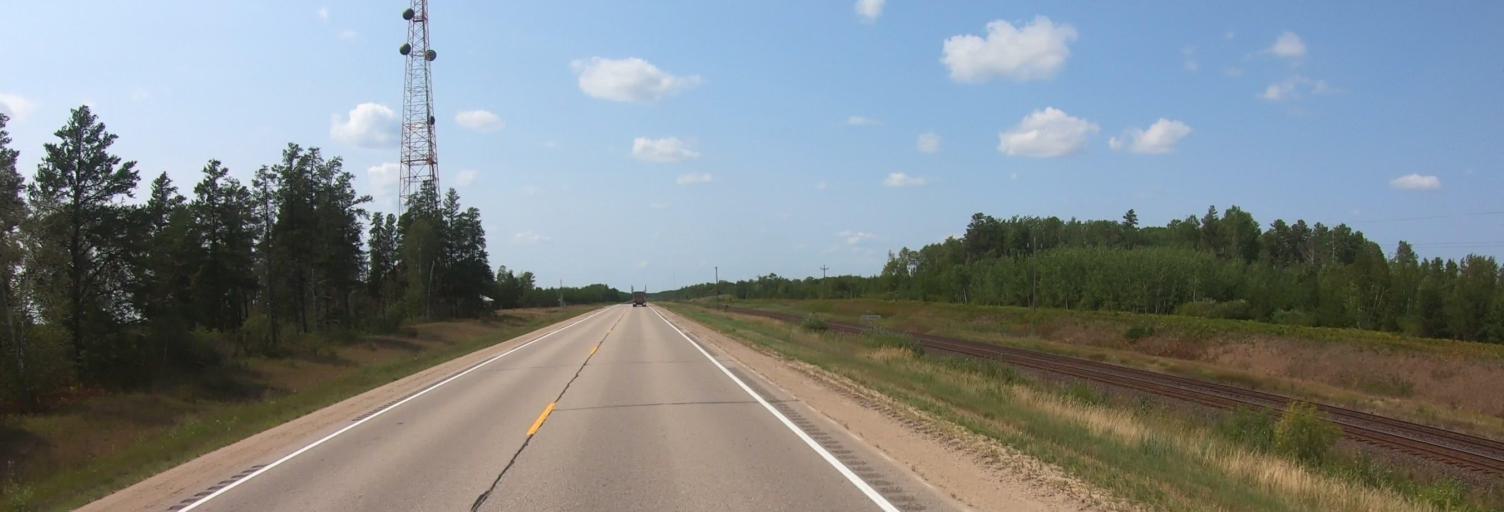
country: US
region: Minnesota
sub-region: Roseau County
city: Warroad
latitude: 48.7890
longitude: -95.0478
